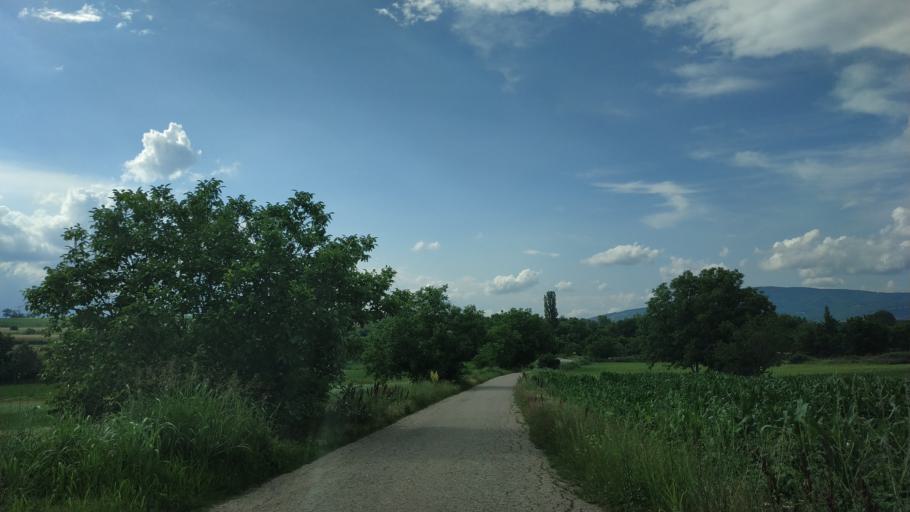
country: RS
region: Central Serbia
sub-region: Nisavski Okrug
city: Aleksinac
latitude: 43.6113
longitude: 21.6492
